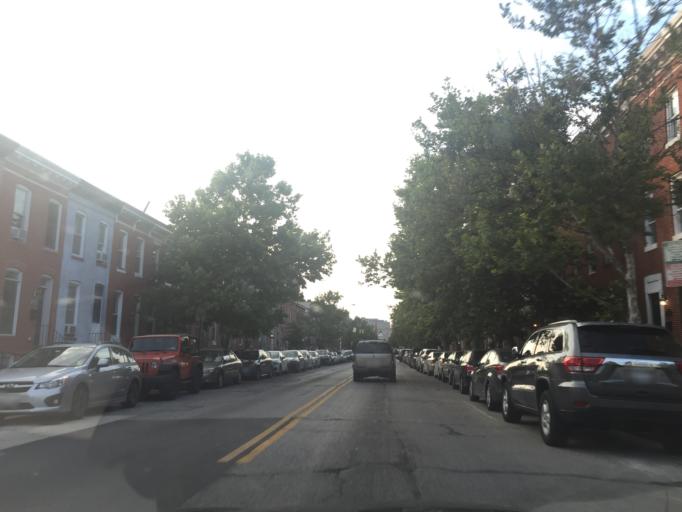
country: US
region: Maryland
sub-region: City of Baltimore
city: Baltimore
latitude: 39.2715
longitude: -76.6151
